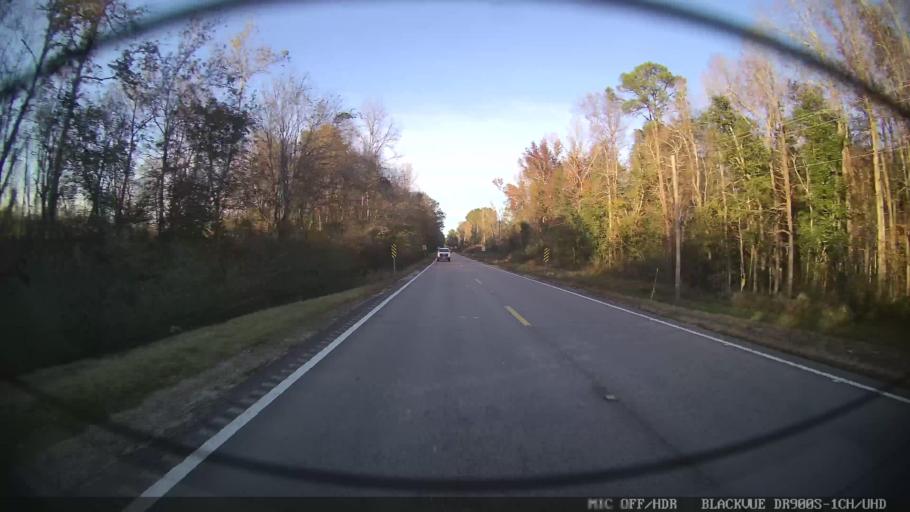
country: US
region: Mississippi
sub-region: Lamar County
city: Lumberton
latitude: 31.0126
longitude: -89.4505
